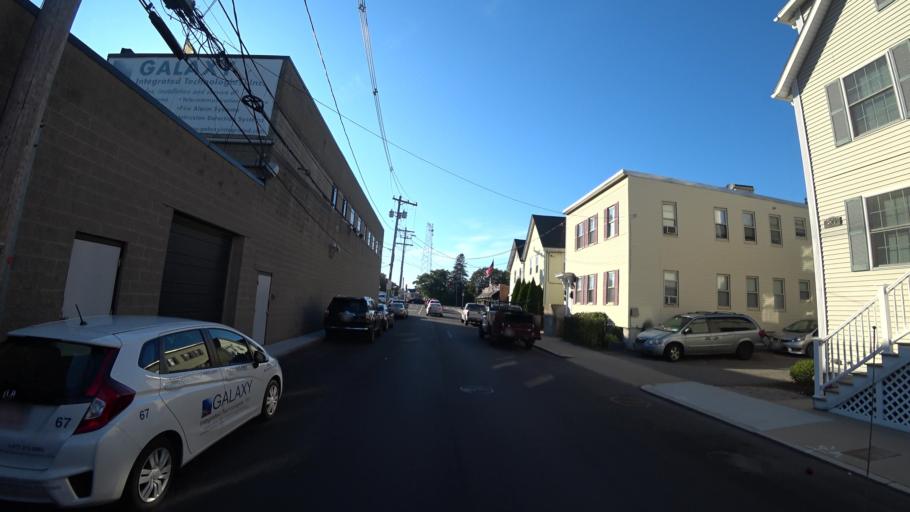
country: US
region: Massachusetts
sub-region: Norfolk County
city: Brookline
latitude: 42.3587
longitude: -71.1463
